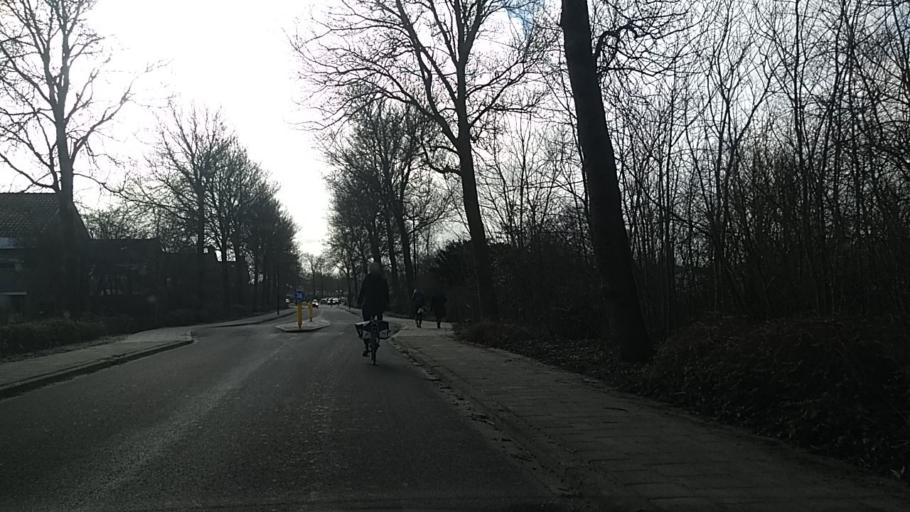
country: NL
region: Friesland
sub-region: Gemeente Harlingen
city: Harlingen
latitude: 53.1704
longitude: 5.4385
